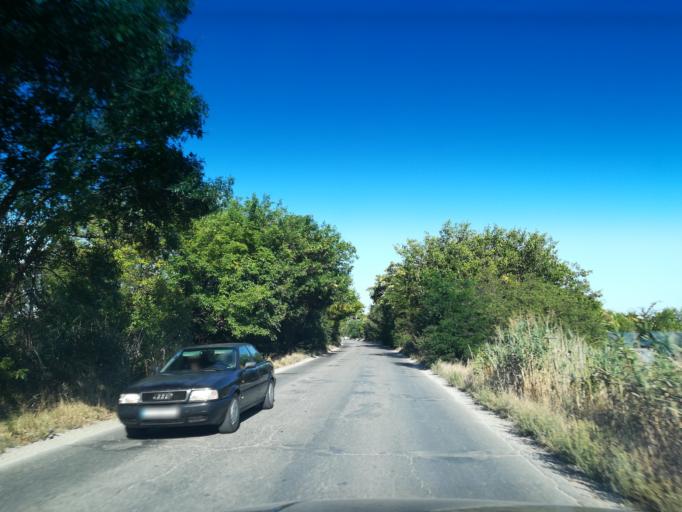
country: BG
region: Plovdiv
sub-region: Obshtina Plovdiv
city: Plovdiv
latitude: 42.1657
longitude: 24.8039
